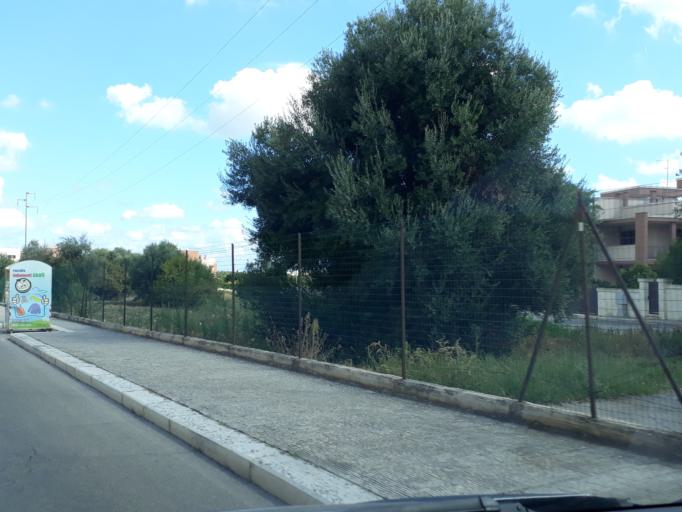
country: IT
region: Apulia
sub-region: Provincia di Brindisi
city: Fasano
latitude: 40.8270
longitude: 17.3626
